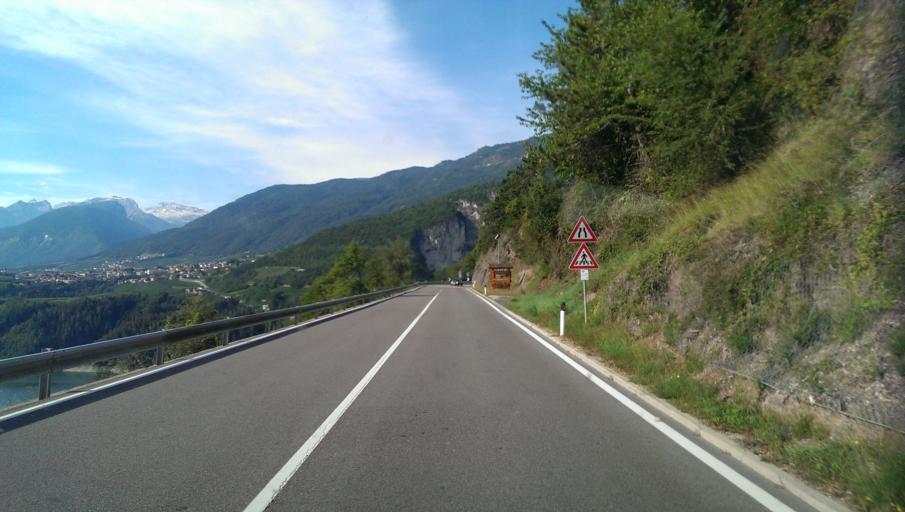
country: IT
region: Trentino-Alto Adige
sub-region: Provincia di Trento
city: Cagno
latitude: 46.3928
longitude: 11.0472
